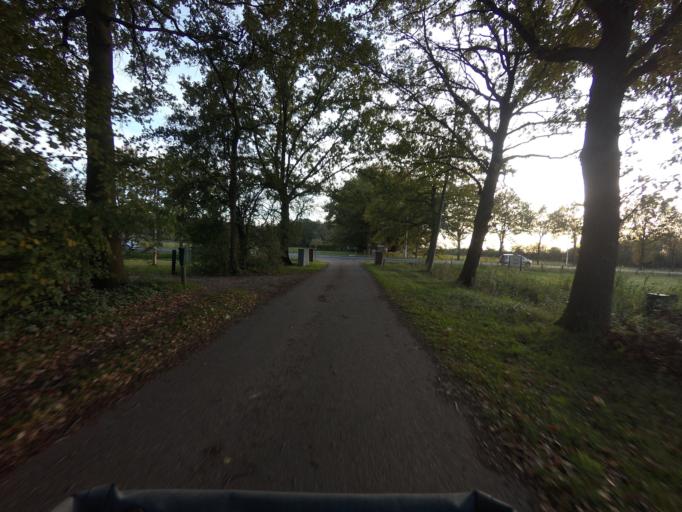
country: NL
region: Utrecht
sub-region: Gemeente De Bilt
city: De Bilt
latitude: 52.1398
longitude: 5.1731
